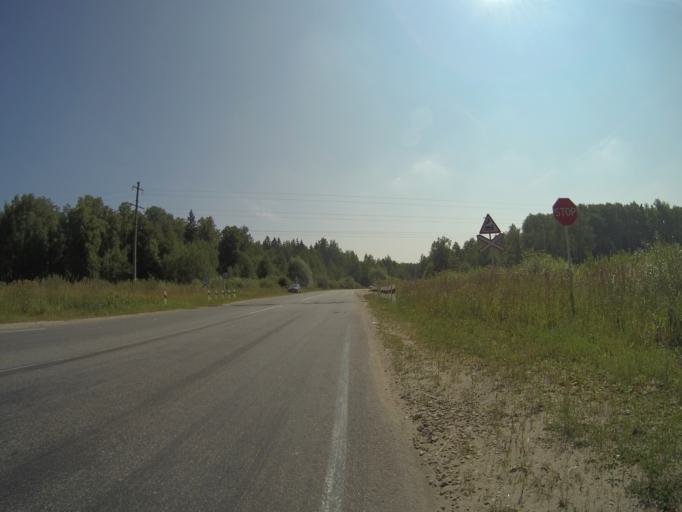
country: RU
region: Vladimir
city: Anopino
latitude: 55.7472
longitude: 40.6813
